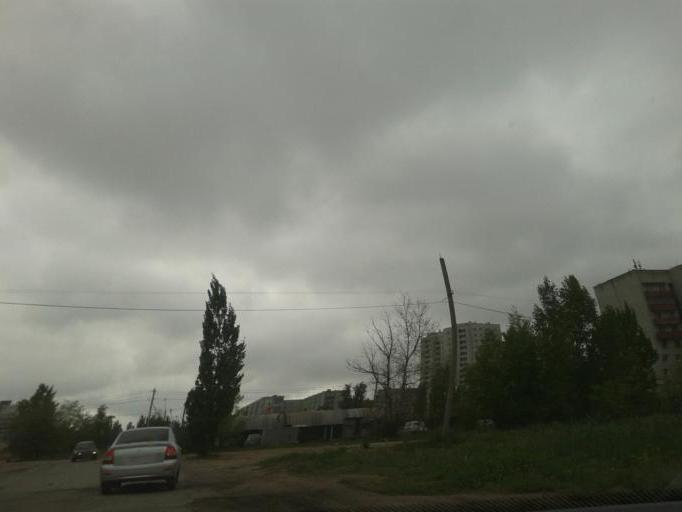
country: RU
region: Volgograd
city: Volgograd
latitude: 48.7612
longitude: 44.4981
